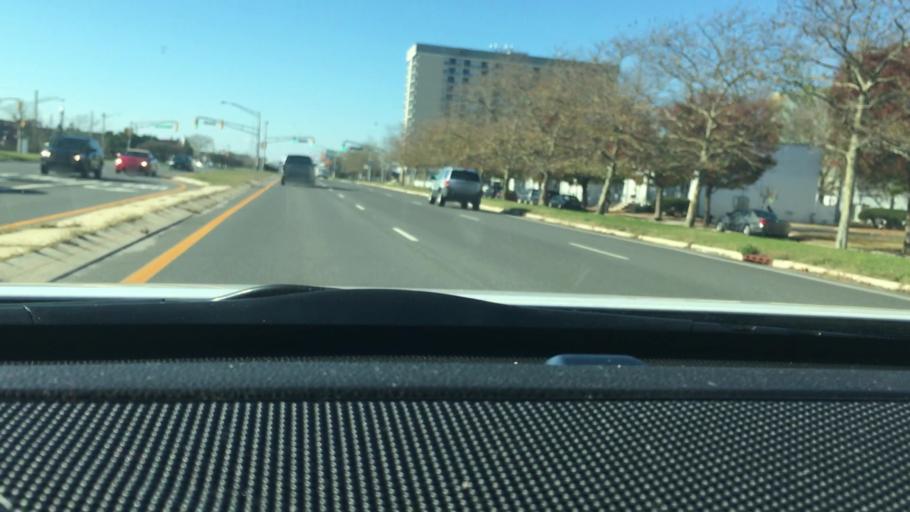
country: US
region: New Jersey
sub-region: Atlantic County
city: Atlantic City
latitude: 39.3697
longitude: -74.4273
